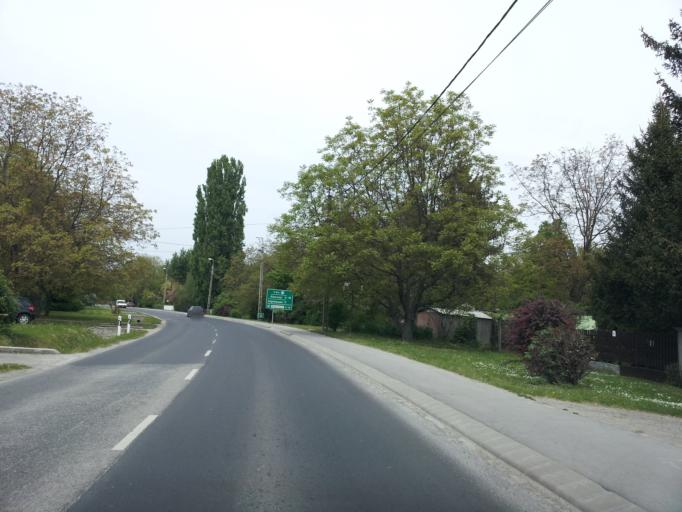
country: HU
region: Pest
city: Tahitotfalu
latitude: 47.7476
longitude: 19.0818
